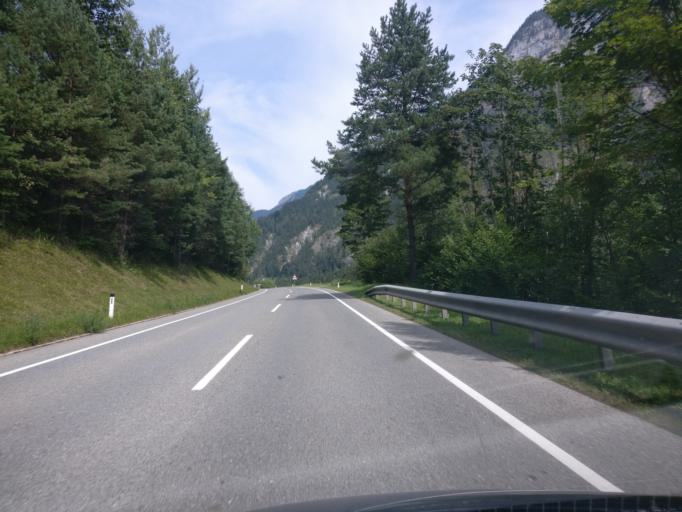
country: AT
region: Salzburg
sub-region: Politischer Bezirk Sankt Johann im Pongau
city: Werfen
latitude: 47.5083
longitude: 13.1667
